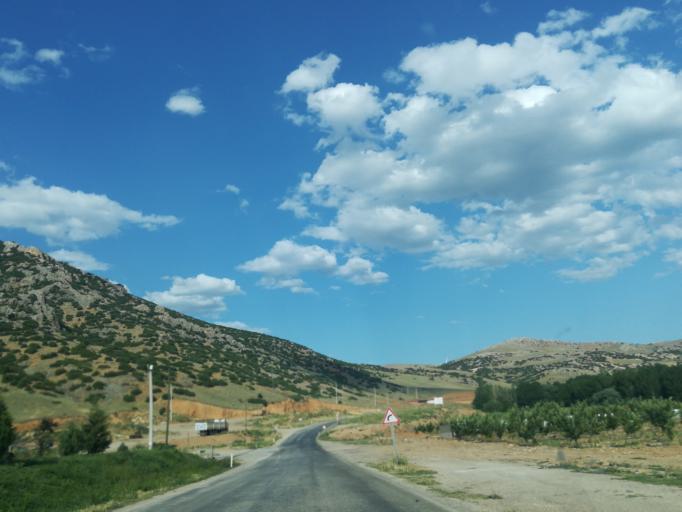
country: TR
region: Afyonkarahisar
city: Dinar
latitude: 38.0993
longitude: 30.1495
